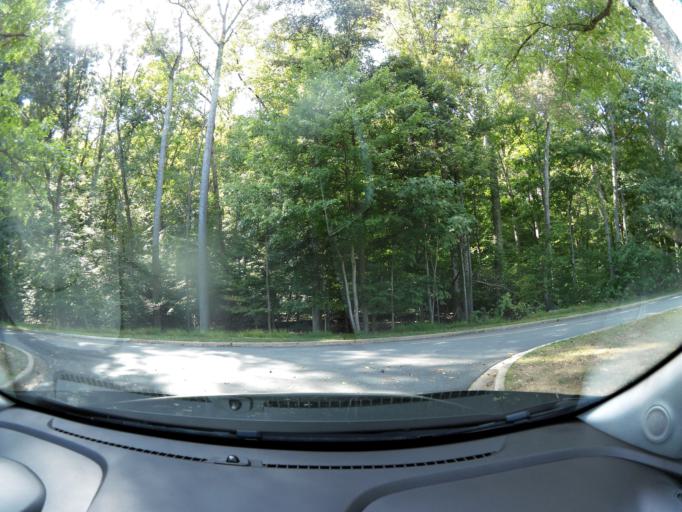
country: US
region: Virginia
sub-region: Fairfax County
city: Great Falls
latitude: 38.9983
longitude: -77.2561
